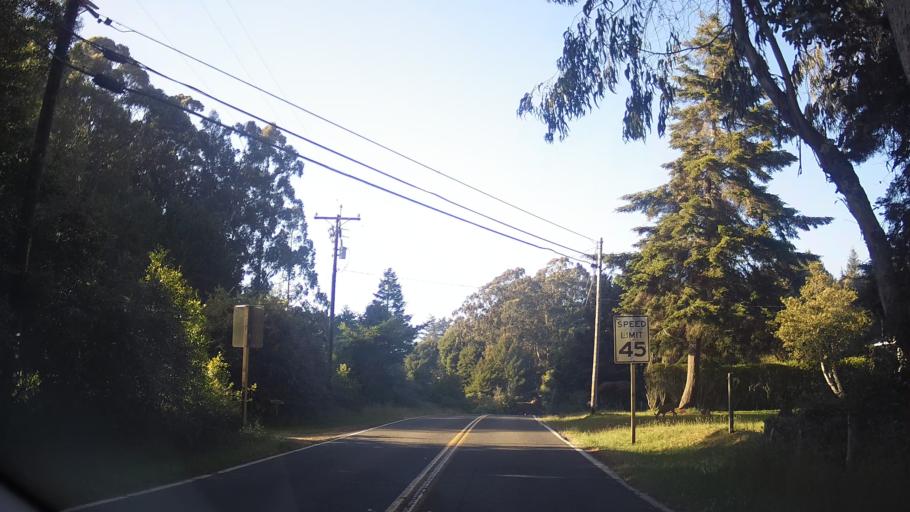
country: US
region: California
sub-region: Mendocino County
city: Fort Bragg
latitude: 39.5206
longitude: -123.7616
